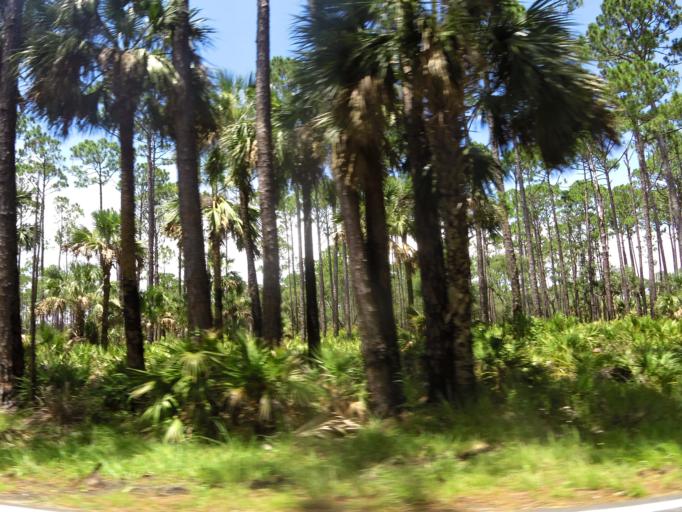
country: US
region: Florida
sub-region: Volusia County
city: Ormond-by-the-Sea
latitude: 29.3559
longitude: -81.1104
